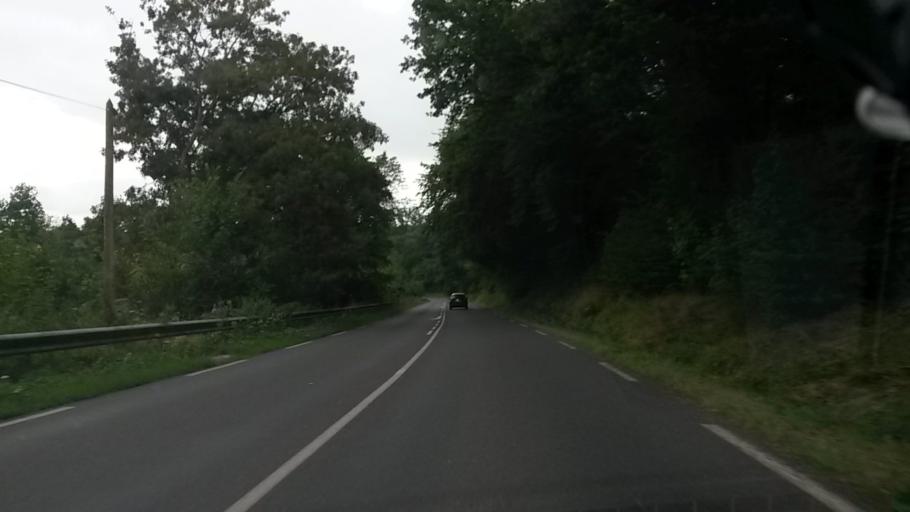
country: FR
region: Haute-Normandie
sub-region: Departement de la Seine-Maritime
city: Aumale
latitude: 49.7658
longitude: 1.7782
